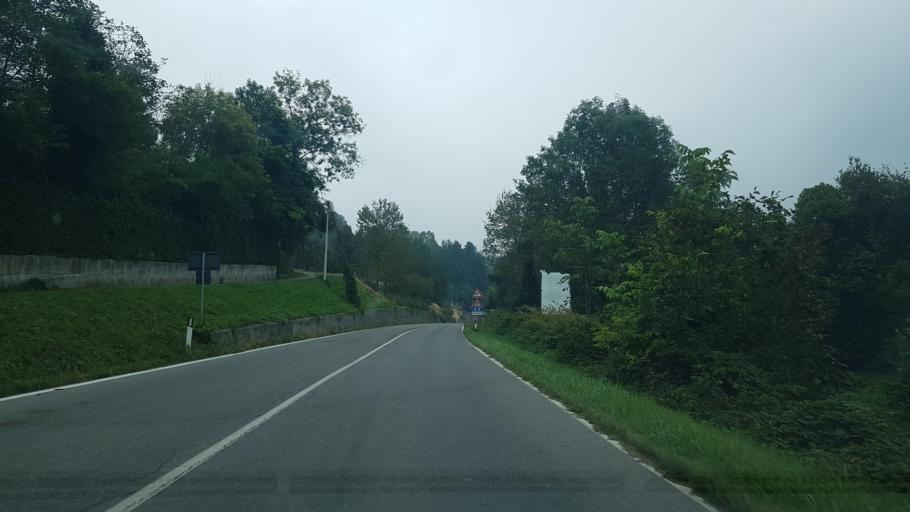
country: IT
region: Piedmont
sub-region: Provincia di Cuneo
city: Frabosa Sottana
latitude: 44.3268
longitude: 7.7958
